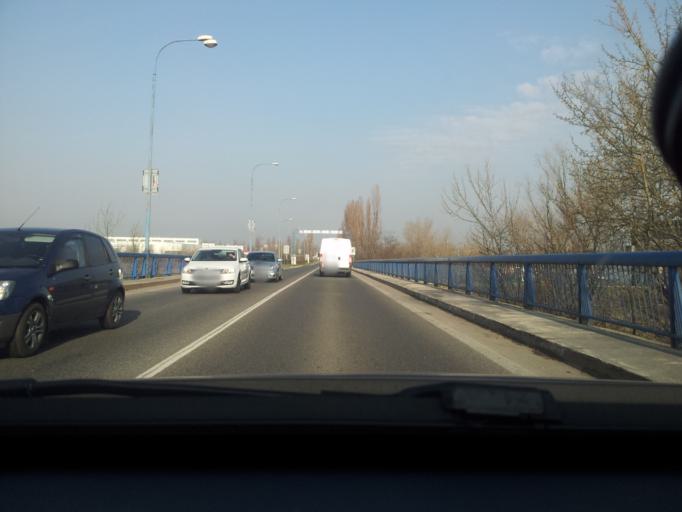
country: SK
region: Trnavsky
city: Hlohovec
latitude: 48.4305
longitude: 17.7910
